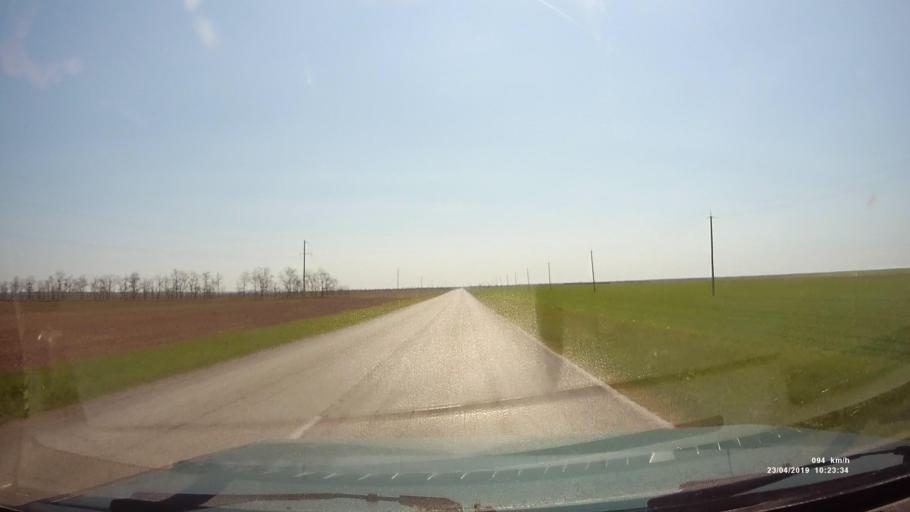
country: RU
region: Rostov
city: Sovetskoye
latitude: 46.6463
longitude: 42.4269
